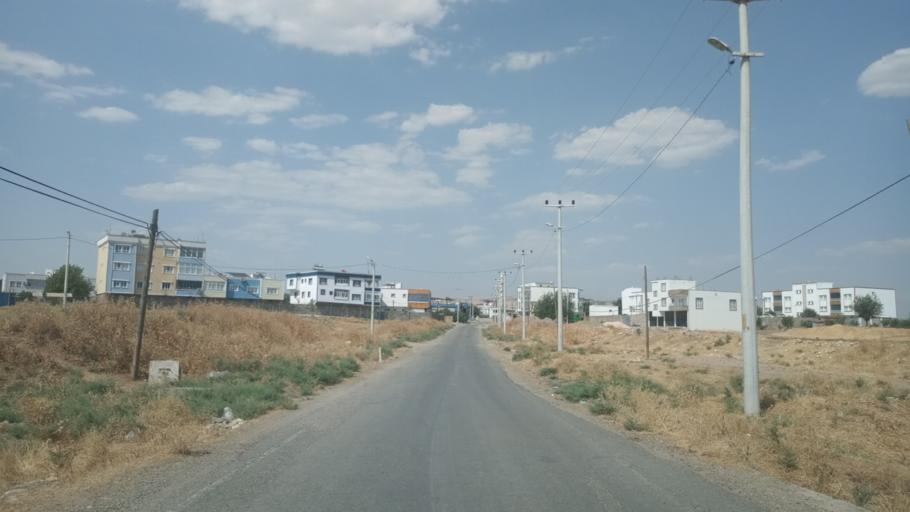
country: TR
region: Batman
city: Binatli
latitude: 37.8437
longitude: 41.2129
